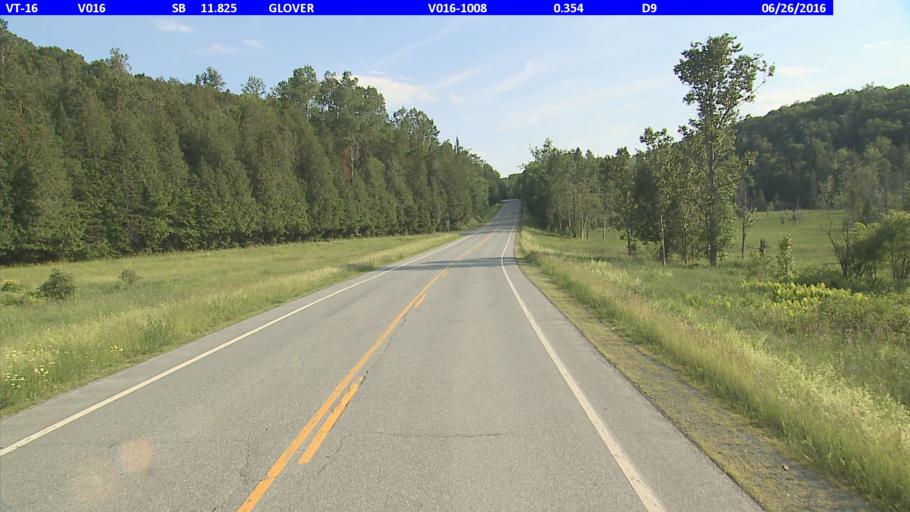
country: US
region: Vermont
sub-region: Caledonia County
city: Hardwick
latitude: 44.6330
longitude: -72.2118
